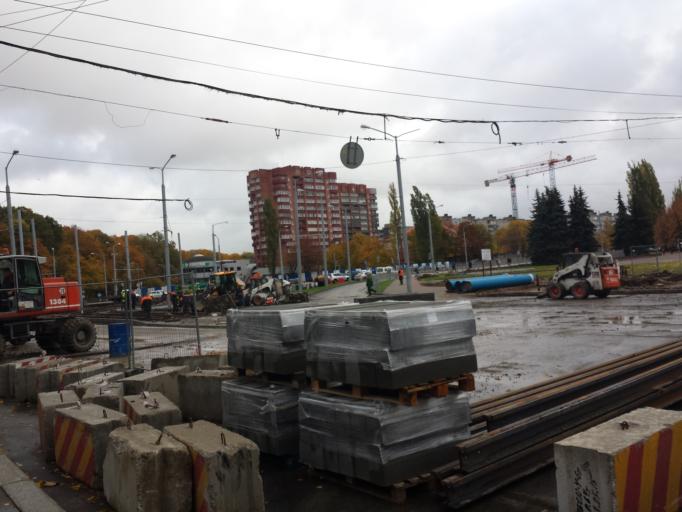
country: RU
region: Kaliningrad
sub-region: Gorod Kaliningrad
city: Kaliningrad
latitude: 54.7217
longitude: 20.5238
